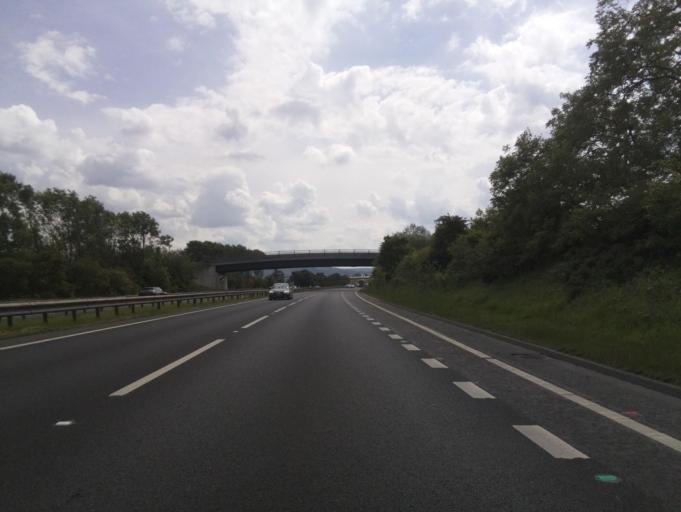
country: GB
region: England
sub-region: Stockton-on-Tees
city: Yarm
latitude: 54.4292
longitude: -1.3211
